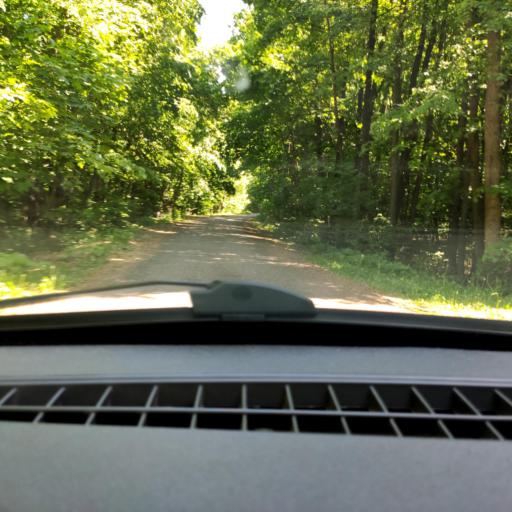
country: RU
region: Bashkortostan
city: Kabakovo
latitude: 54.4291
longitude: 55.9172
